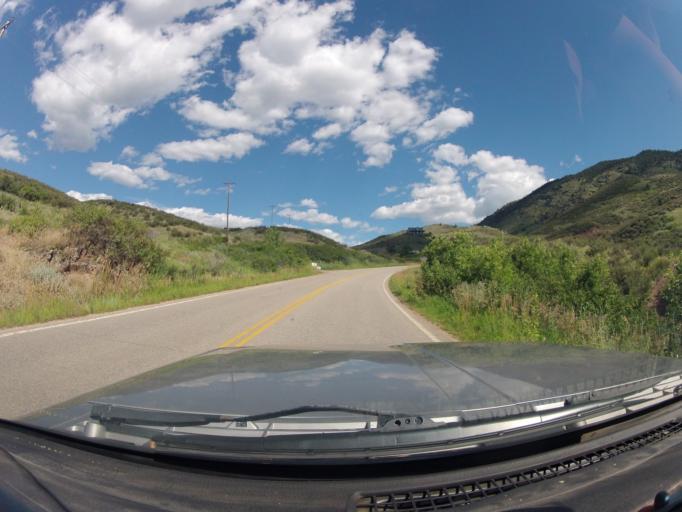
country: US
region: Colorado
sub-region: Larimer County
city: Laporte
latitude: 40.5280
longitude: -105.2644
